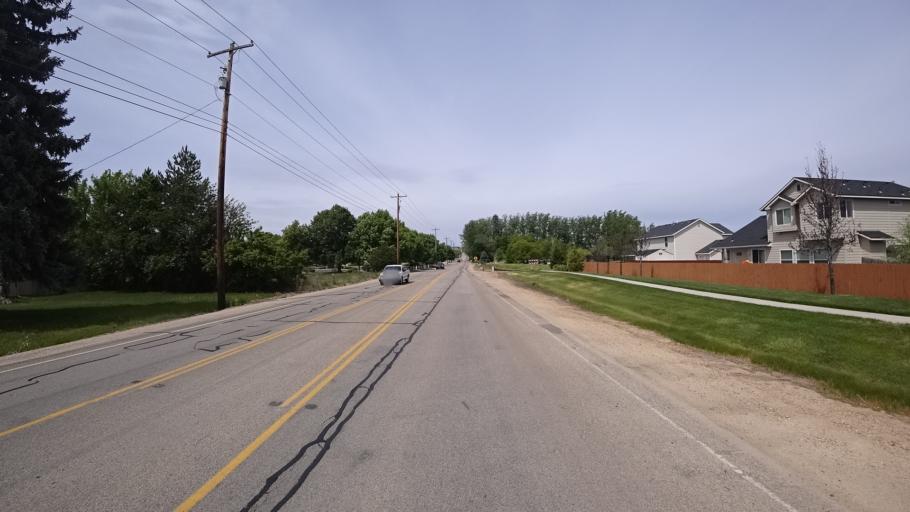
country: US
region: Idaho
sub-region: Ada County
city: Meridian
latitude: 43.5612
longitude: -116.3711
